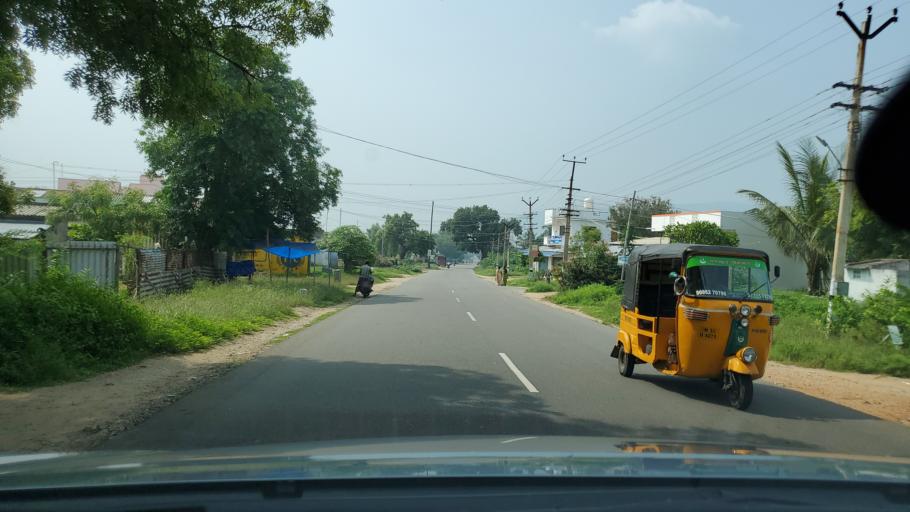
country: IN
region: Tamil Nadu
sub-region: Erode
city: Chennimalai
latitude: 11.1810
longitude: 77.6080
